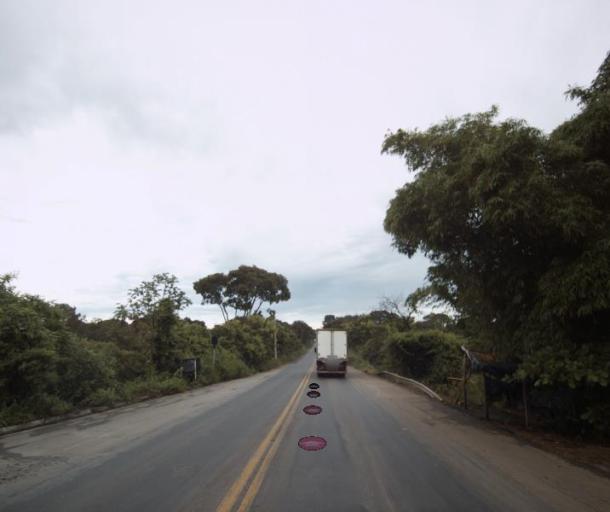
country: BR
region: Goias
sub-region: Porangatu
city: Porangatu
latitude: -13.7162
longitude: -49.0212
